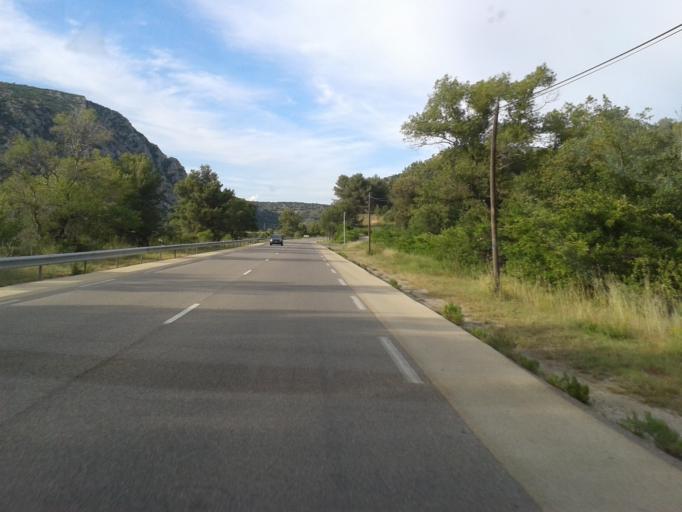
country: FR
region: Provence-Alpes-Cote d'Azur
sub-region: Departement des Bouches-du-Rhone
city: Jouques
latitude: 43.6724
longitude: 5.6496
